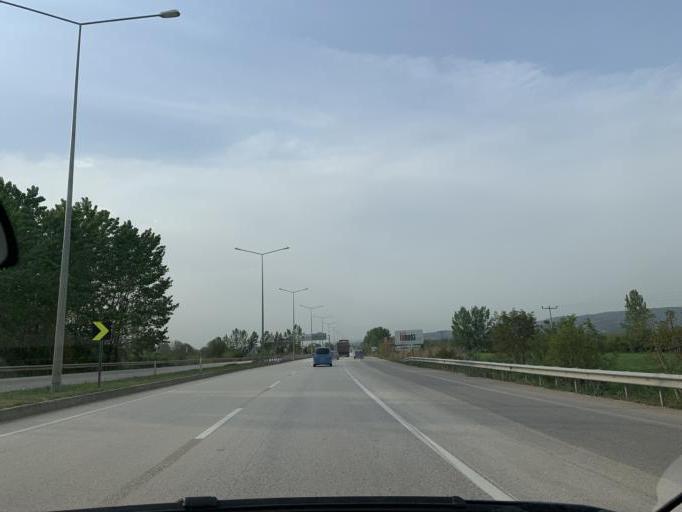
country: TR
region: Bursa
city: Kursunlu
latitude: 40.0439
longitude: 29.5916
